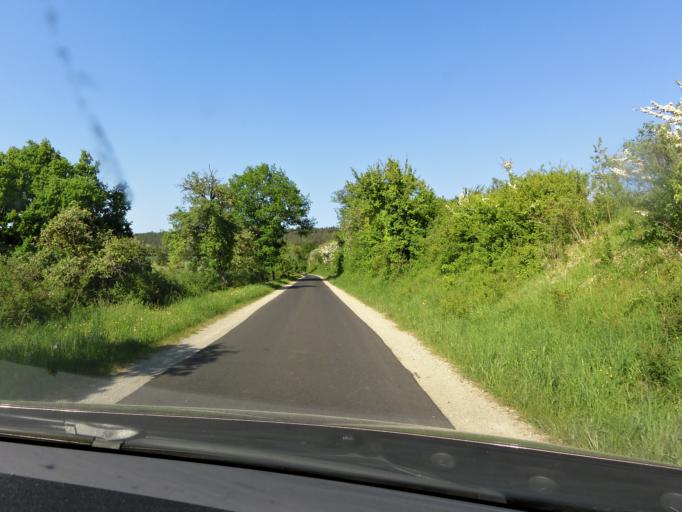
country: DE
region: Thuringia
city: Lauterbach
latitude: 51.0714
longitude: 10.3528
